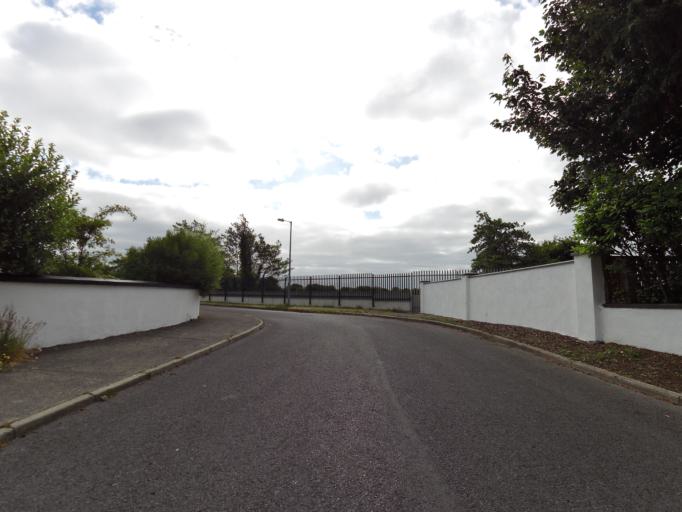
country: IE
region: Connaught
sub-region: County Galway
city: Athenry
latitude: 53.3020
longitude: -8.7407
